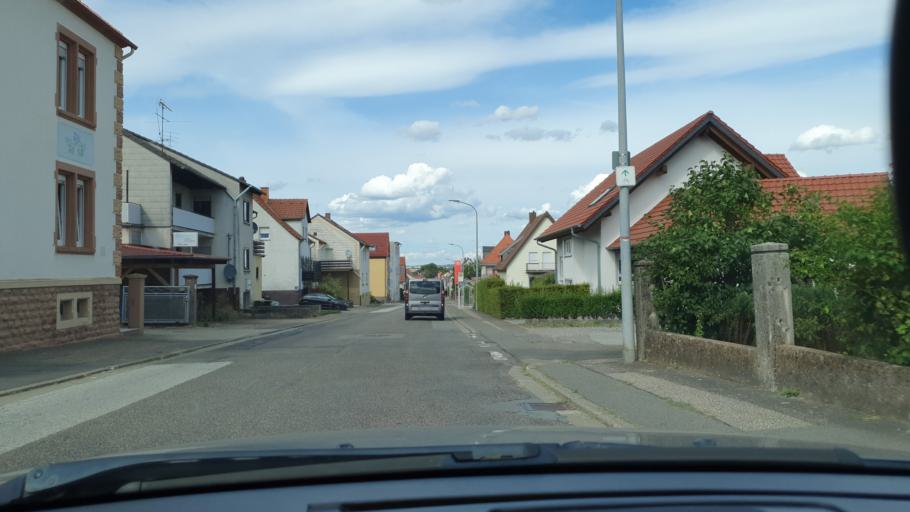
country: DE
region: Rheinland-Pfalz
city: Hohfroschen
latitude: 49.2439
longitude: 7.5611
